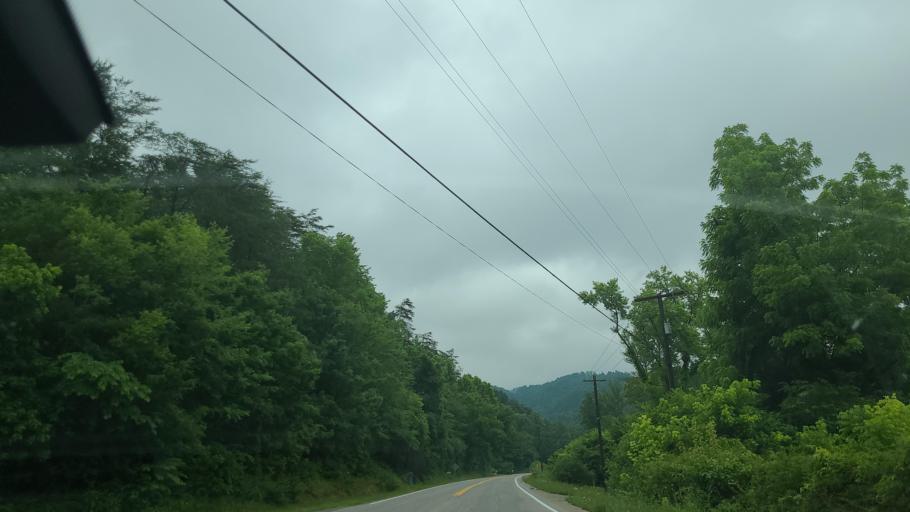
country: US
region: Tennessee
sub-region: Anderson County
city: Oak Ridge
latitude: 36.0886
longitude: -84.2765
